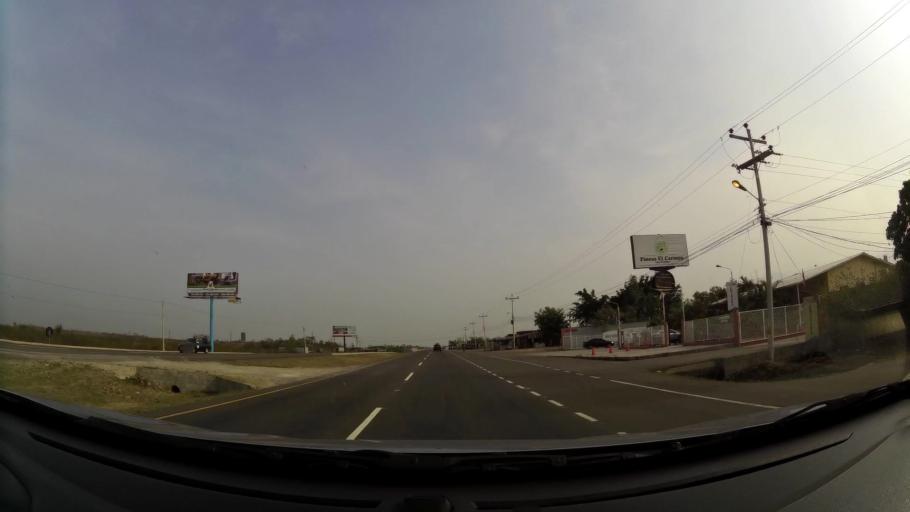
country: HN
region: Comayagua
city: Villa de San Antonio
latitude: 14.3410
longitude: -87.5925
